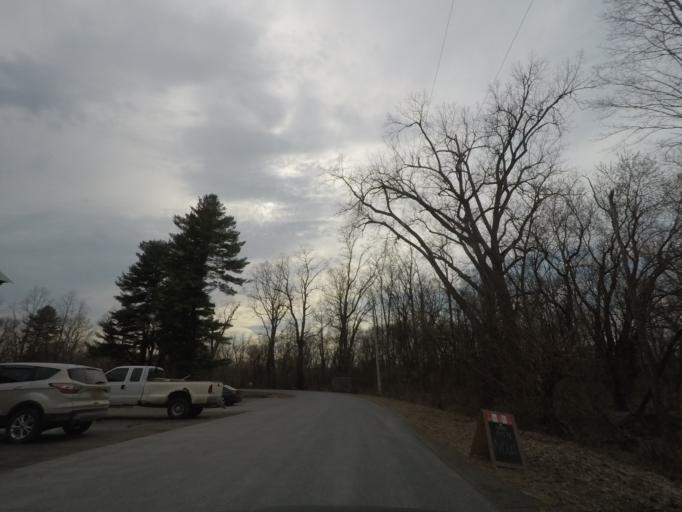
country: US
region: New York
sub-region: Saratoga County
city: Schuylerville
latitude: 43.1001
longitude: -73.5700
